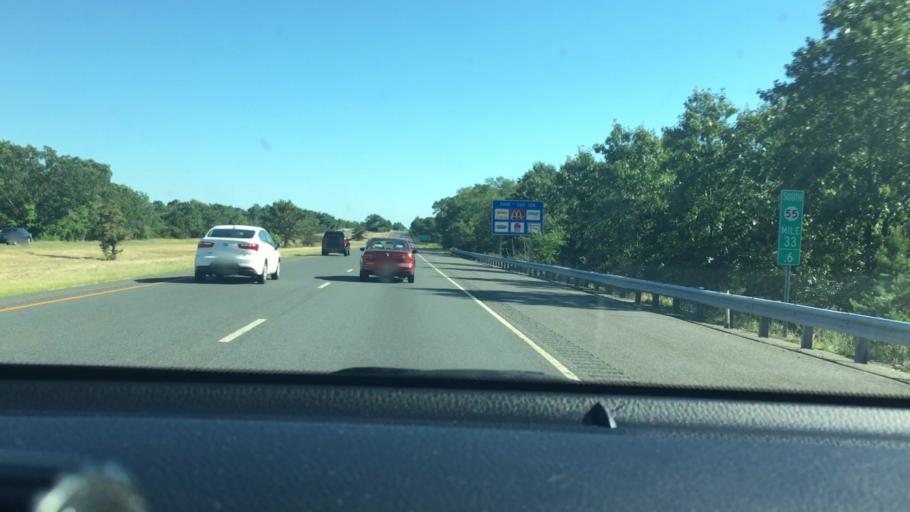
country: US
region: New Jersey
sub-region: Cumberland County
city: Vineland
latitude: 39.5017
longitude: -75.0700
